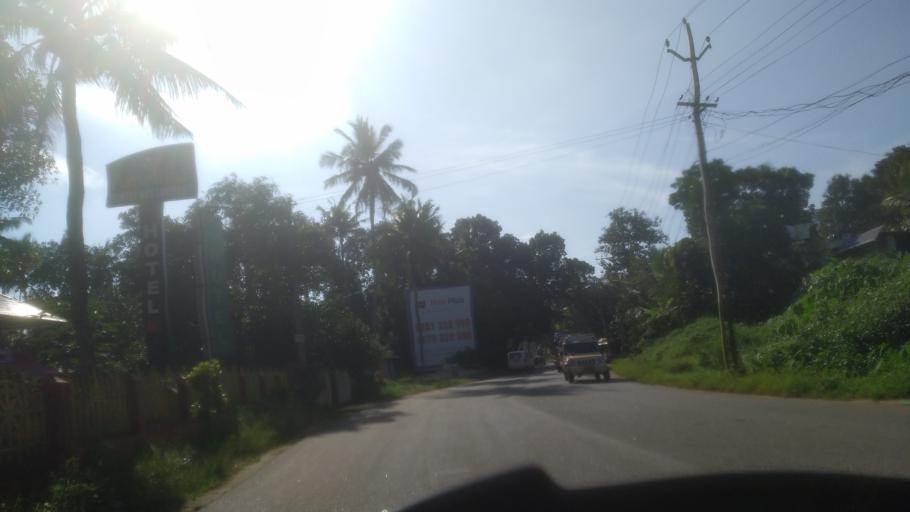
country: IN
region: Kerala
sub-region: Ernakulam
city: Muvattupuzha
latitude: 9.9805
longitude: 76.5449
